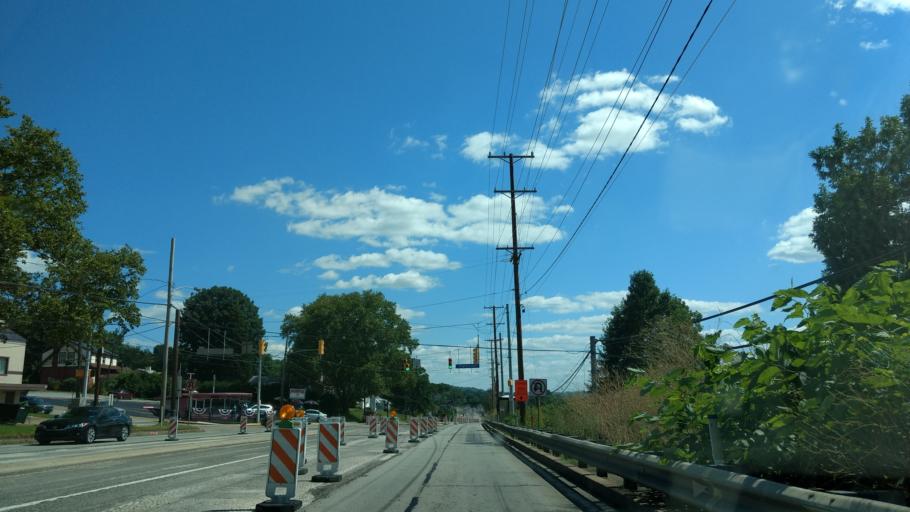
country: US
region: Pennsylvania
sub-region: Beaver County
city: Aliquippa
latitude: 40.6465
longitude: -80.2336
